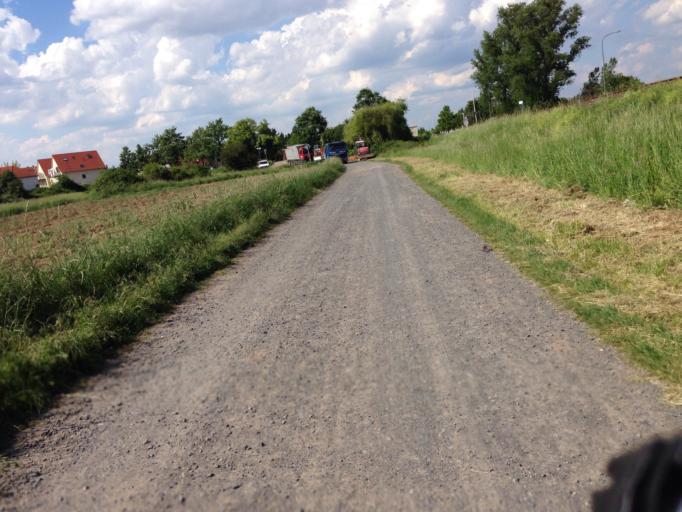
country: DE
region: Hesse
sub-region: Regierungsbezirk Darmstadt
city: Hanau am Main
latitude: 50.0922
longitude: 8.9340
